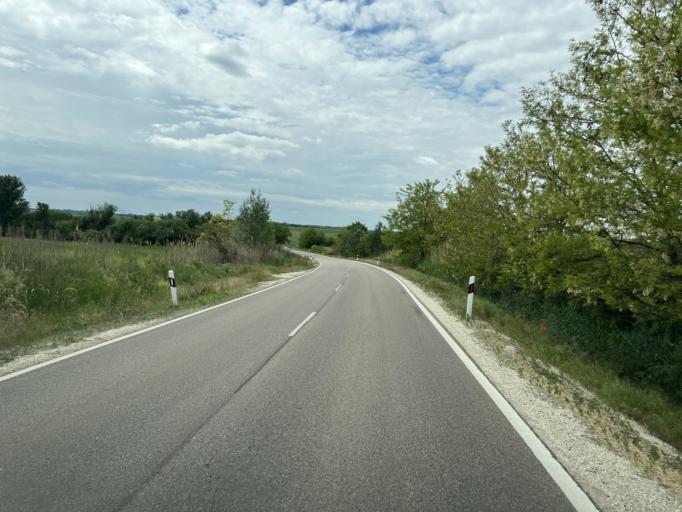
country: HU
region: Pest
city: Zsambok
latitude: 47.5249
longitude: 19.5994
